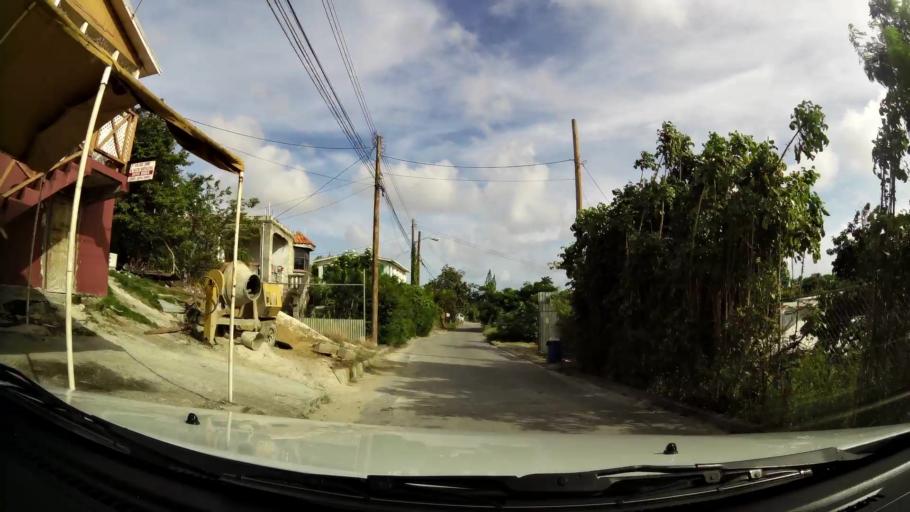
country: BB
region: Saint Michael
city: Bridgetown
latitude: 13.0876
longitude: -59.5898
